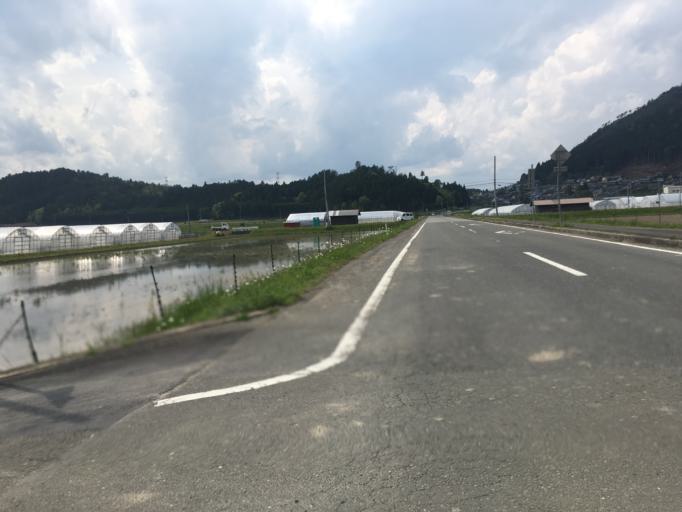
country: JP
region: Kyoto
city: Kameoka
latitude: 35.1041
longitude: 135.5868
